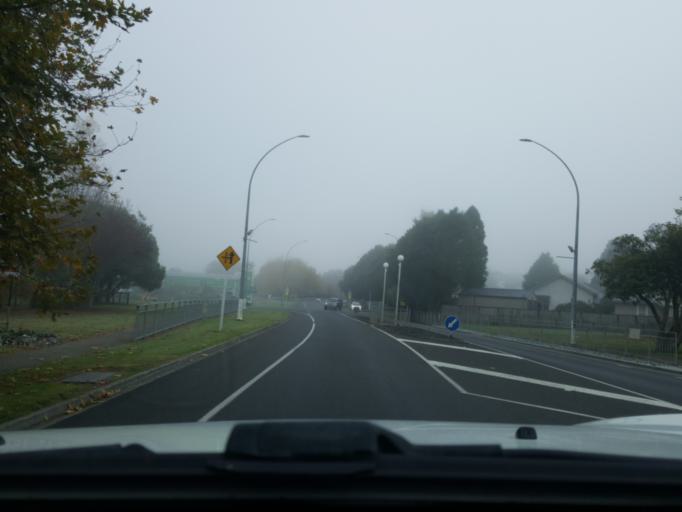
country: NZ
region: Waikato
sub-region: Waikato District
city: Ngaruawahia
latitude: -37.6723
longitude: 175.1533
